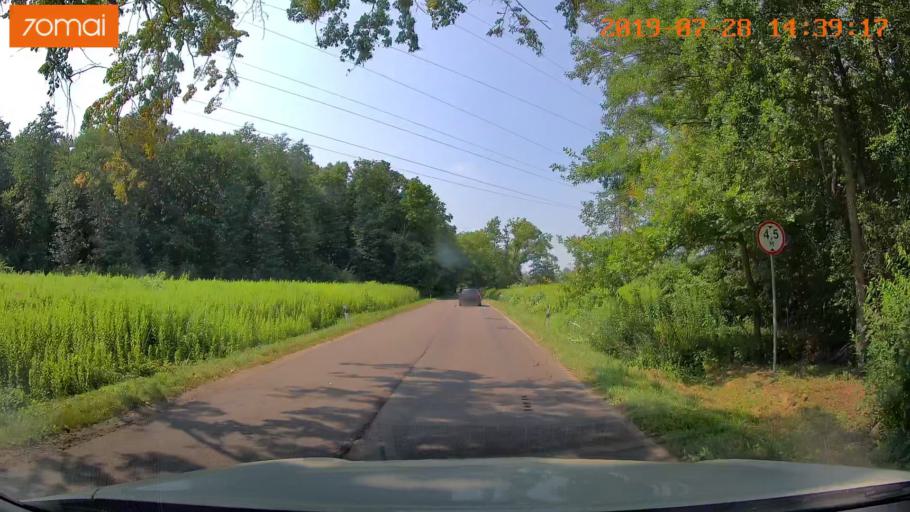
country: RU
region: Kaliningrad
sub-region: Gorod Kaliningrad
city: Yantarnyy
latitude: 54.8471
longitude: 19.9715
